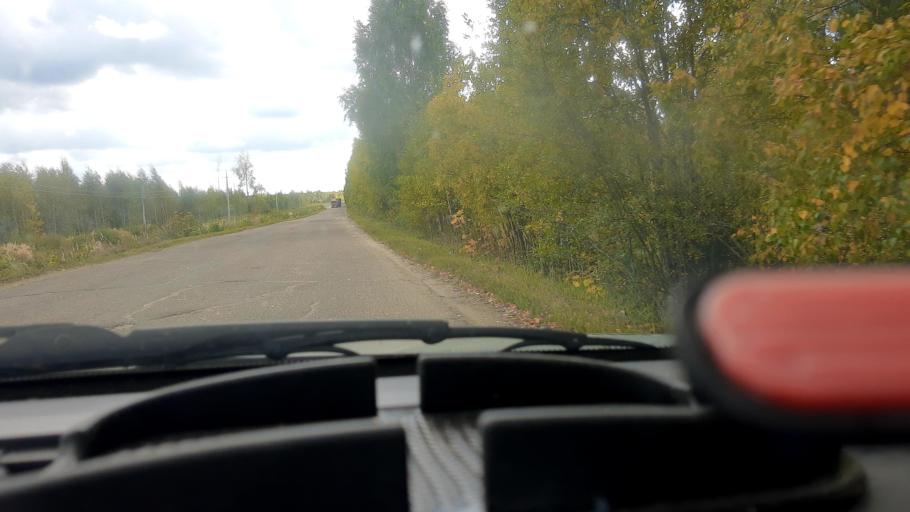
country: RU
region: Mariy-El
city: Kilemary
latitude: 56.8898
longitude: 46.7573
